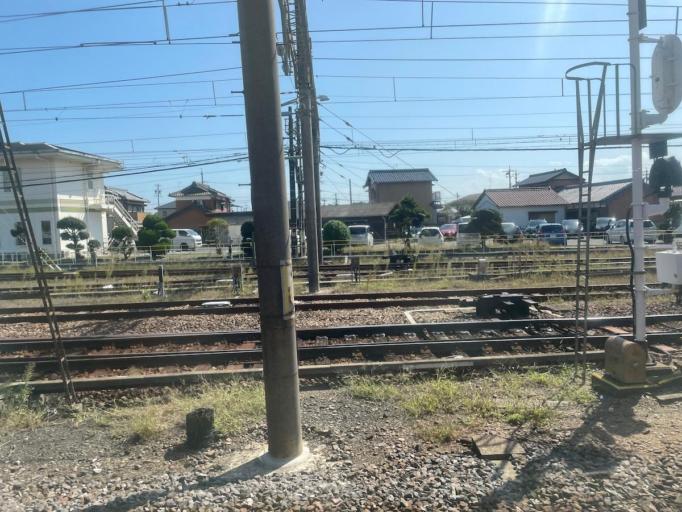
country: JP
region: Mie
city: Kawage
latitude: 34.7710
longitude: 136.5326
